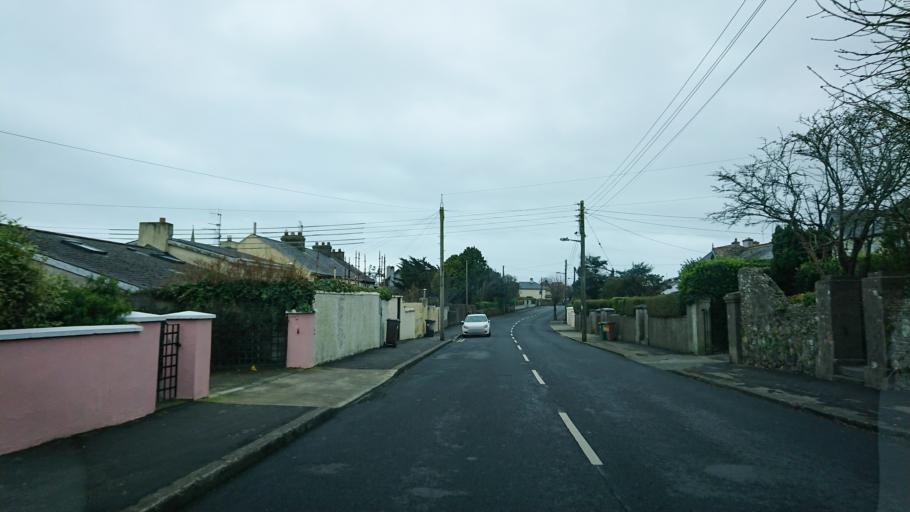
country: IE
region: Munster
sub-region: Waterford
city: Tra Mhor
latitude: 52.1608
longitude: -7.1561
